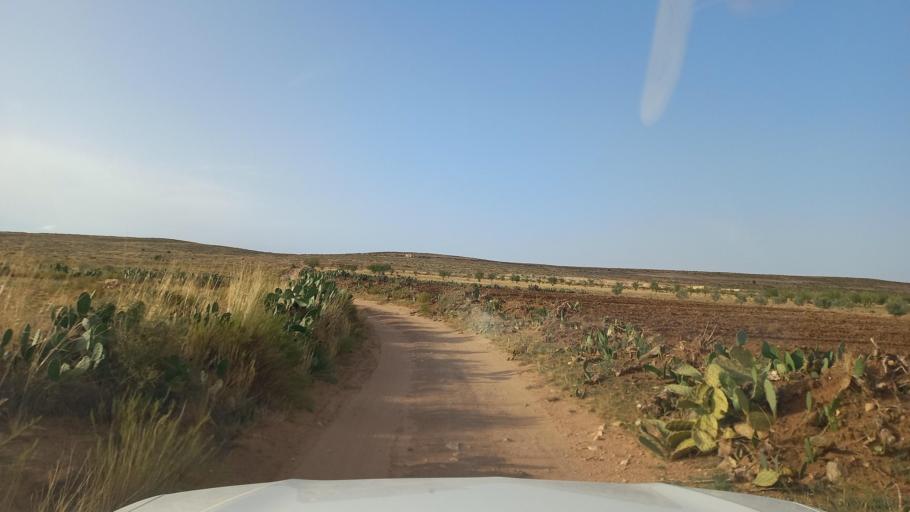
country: TN
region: Al Qasrayn
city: Kasserine
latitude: 35.3581
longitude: 8.8414
